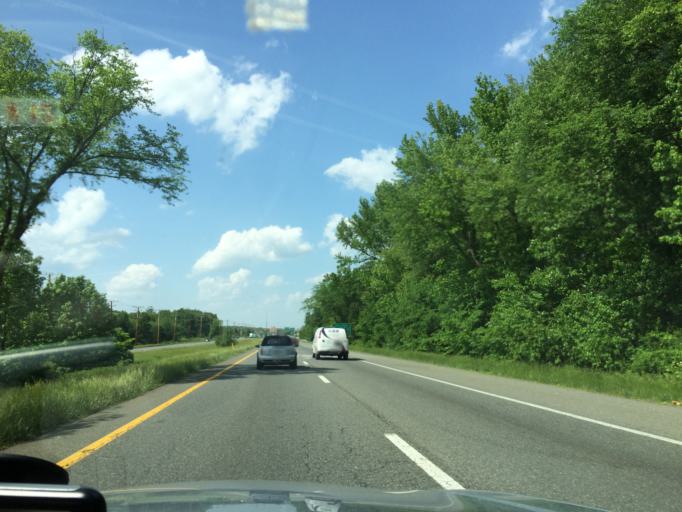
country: US
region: Maryland
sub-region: Prince George's County
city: Bowie
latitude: 38.9375
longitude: -76.7177
